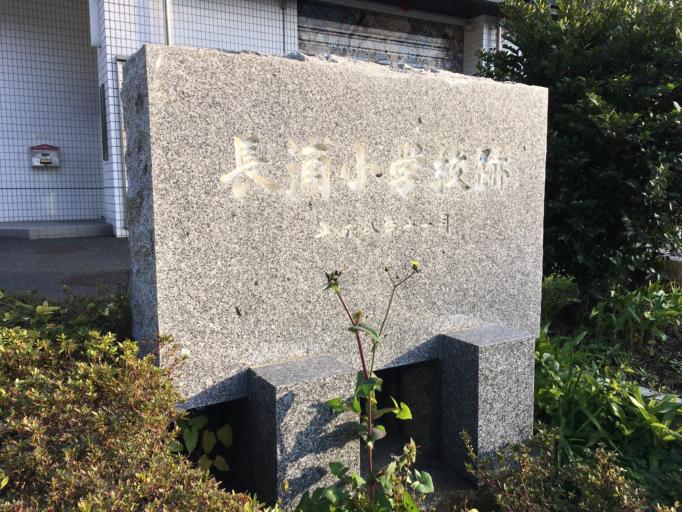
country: JP
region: Kanagawa
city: Yokosuka
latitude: 35.2874
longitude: 139.6428
